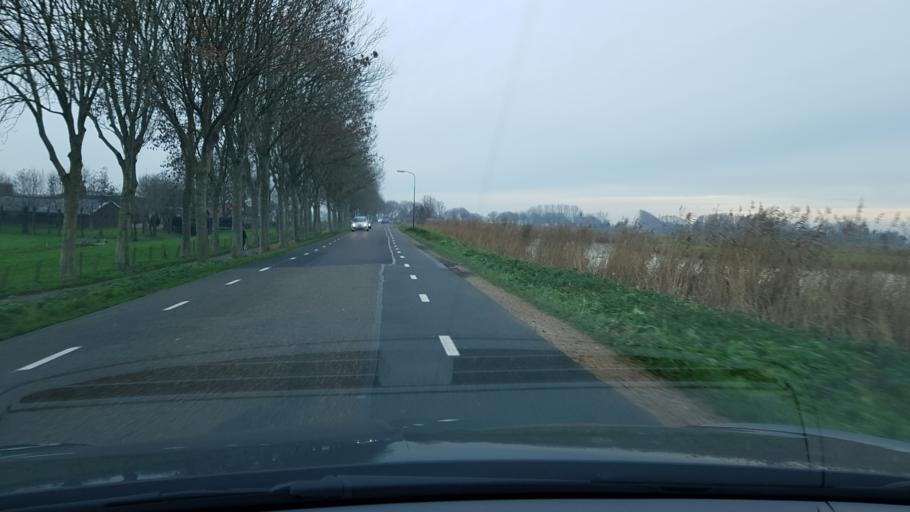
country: NL
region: North Holland
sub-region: Gemeente Uithoorn
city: Uithoorn
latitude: 52.2226
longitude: 4.8290
